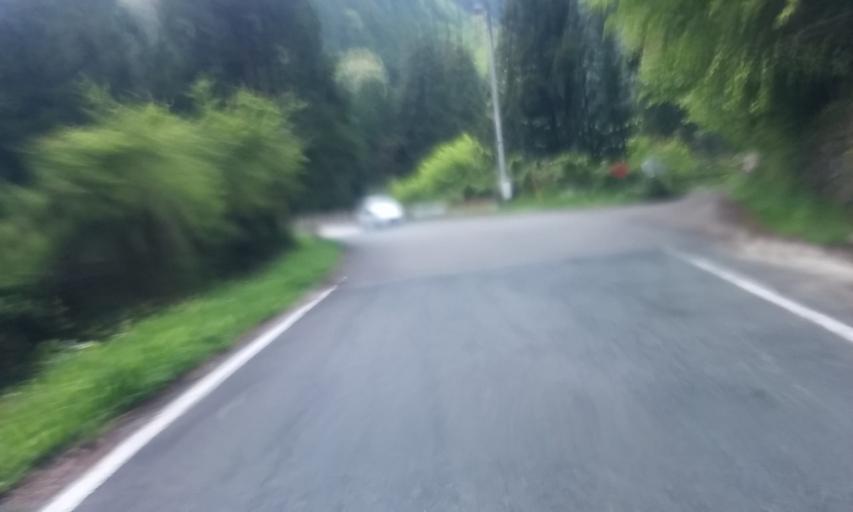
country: JP
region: Ehime
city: Saijo
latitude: 33.7998
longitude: 133.2826
